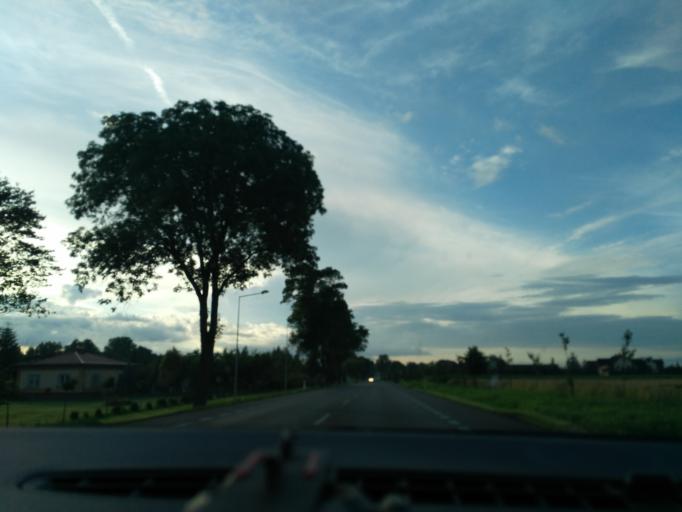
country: PL
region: Lublin Voivodeship
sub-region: Powiat lubelski
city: Niedrzwica Duza
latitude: 51.0839
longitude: 22.3705
